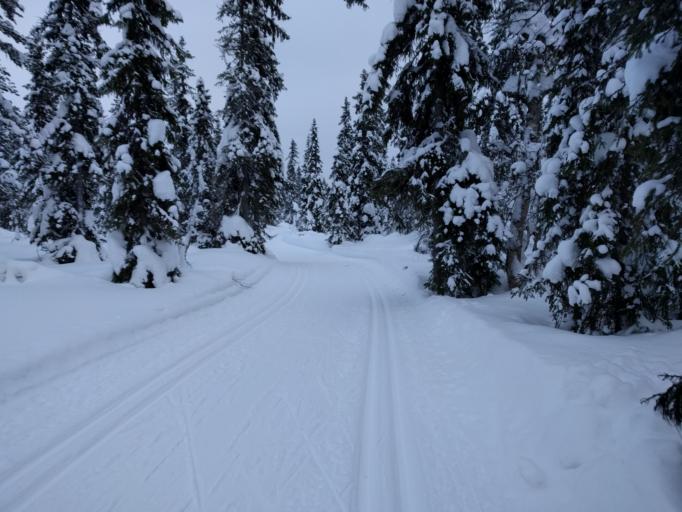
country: NO
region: Hedmark
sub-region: Trysil
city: Innbygda
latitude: 61.1511
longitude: 13.0373
